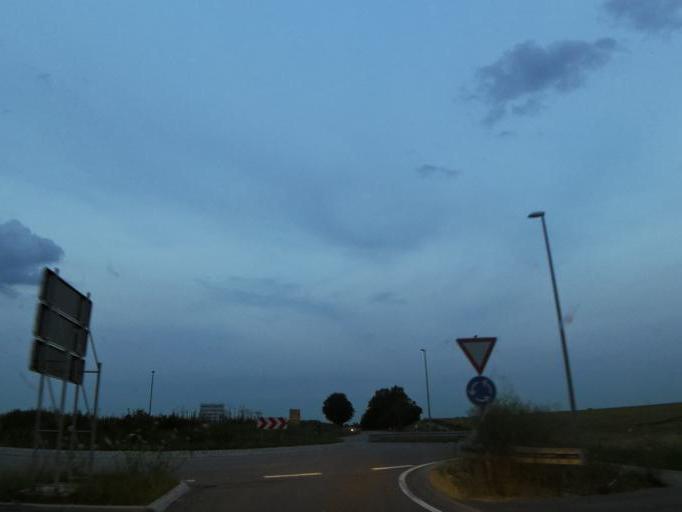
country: DE
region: Bavaria
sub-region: Upper Bavaria
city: Pastetten
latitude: 48.2109
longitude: 11.9532
